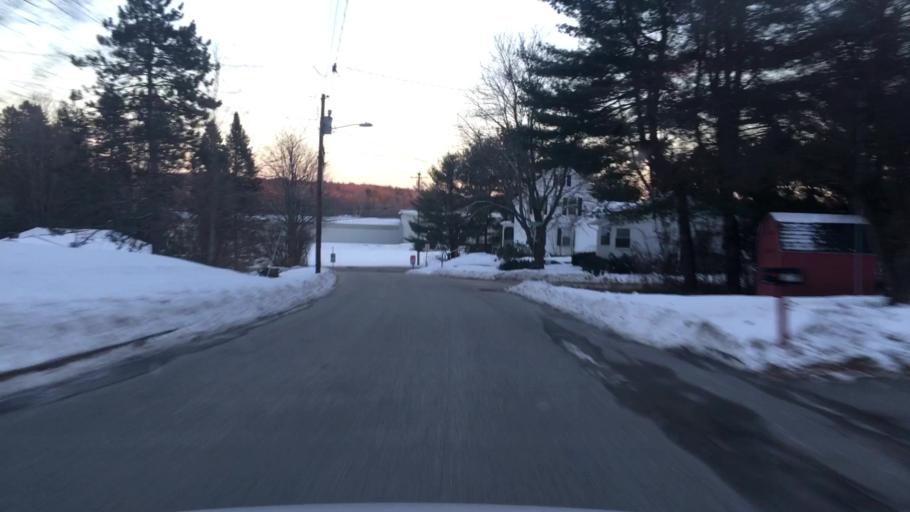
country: US
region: Maine
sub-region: Androscoggin County
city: Auburn
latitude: 44.0776
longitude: -70.2488
